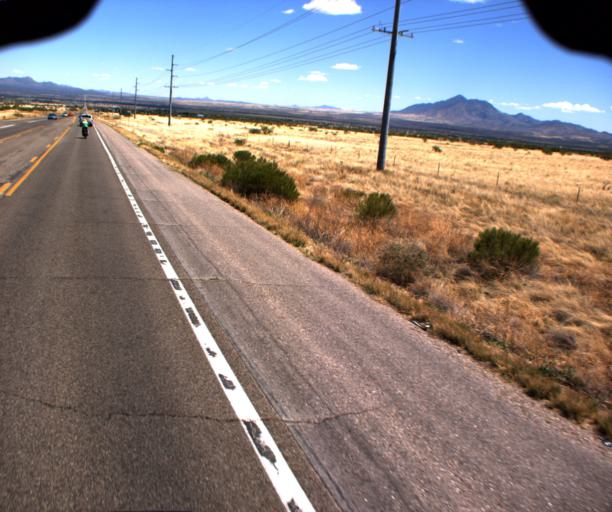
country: US
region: Arizona
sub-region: Cochise County
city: Sierra Vista Southeast
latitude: 31.3799
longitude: -110.2061
